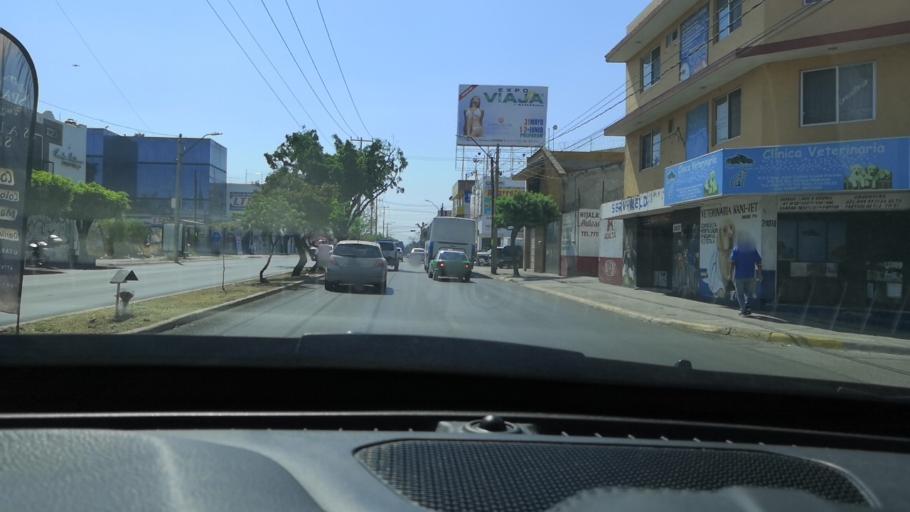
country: MX
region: Guanajuato
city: Leon
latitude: 21.1167
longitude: -101.7007
